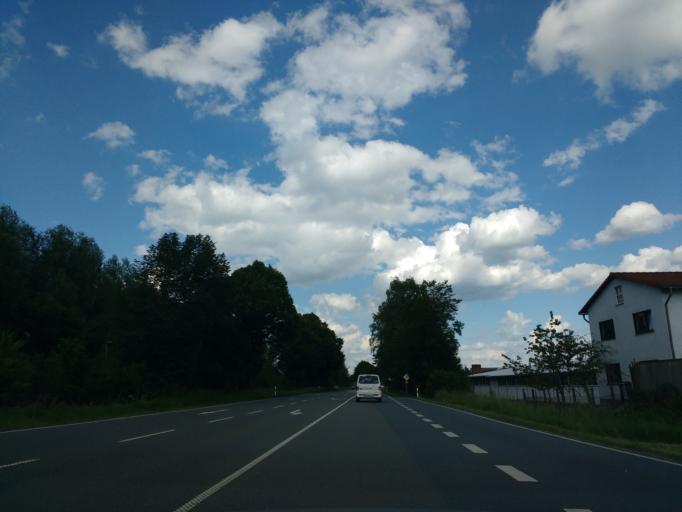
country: DE
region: Hesse
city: Allendorf
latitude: 51.0276
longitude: 8.6898
